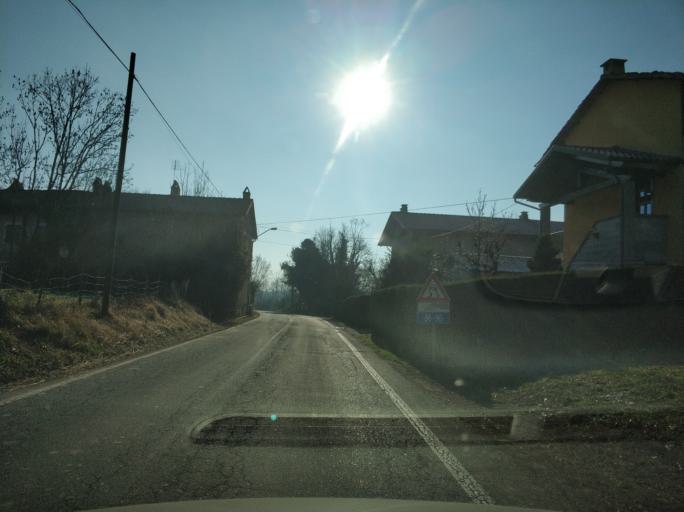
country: IT
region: Piedmont
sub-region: Provincia di Torino
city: Rocca Canavese
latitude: 45.2961
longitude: 7.5806
